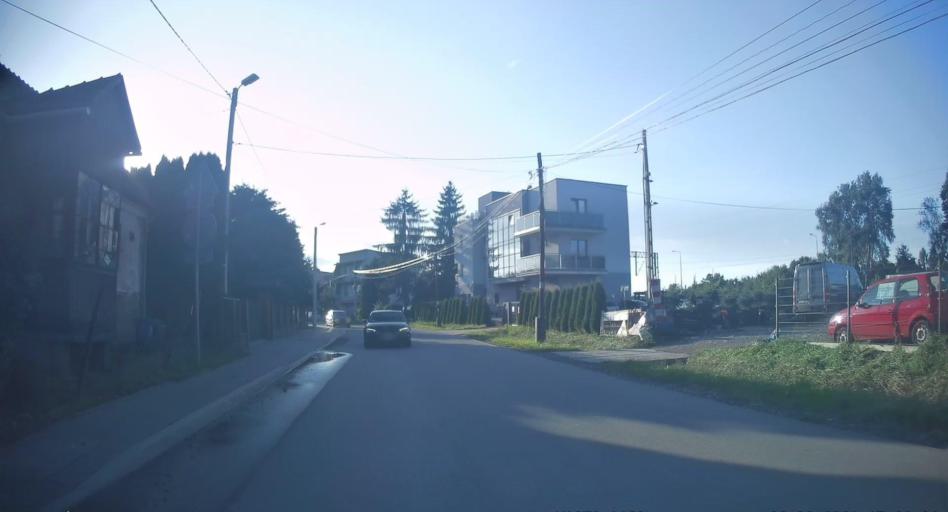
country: PL
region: Lesser Poland Voivodeship
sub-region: Powiat wielicki
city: Czarnochowice
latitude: 50.0191
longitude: 20.0413
